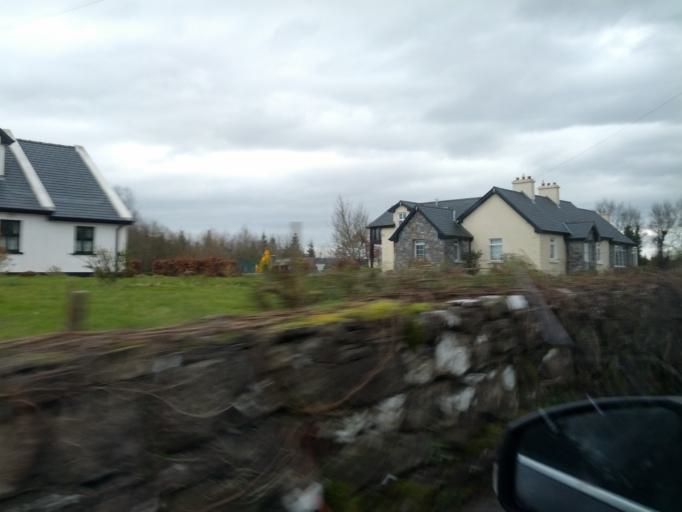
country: IE
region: Connaught
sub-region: County Galway
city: Athenry
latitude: 53.3770
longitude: -8.6277
